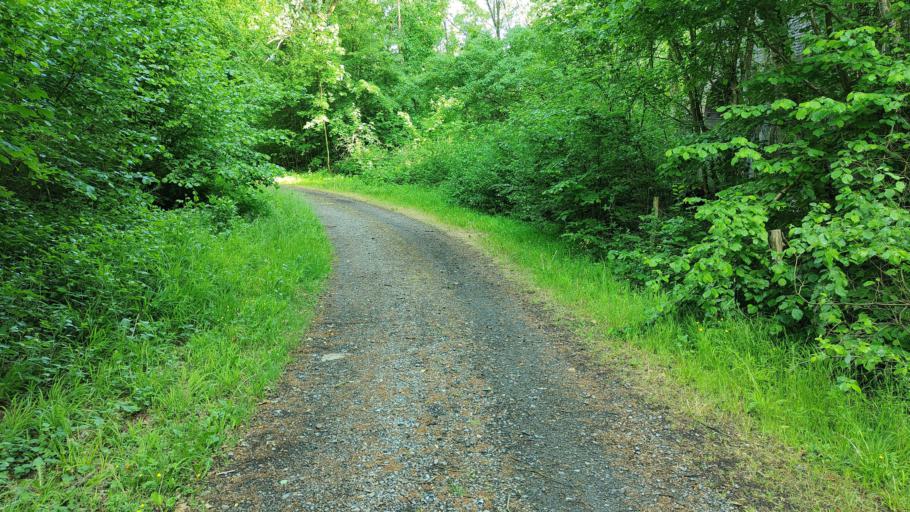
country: BE
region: Wallonia
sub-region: Province de Liege
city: La Calamine
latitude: 50.7056
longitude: 6.0468
